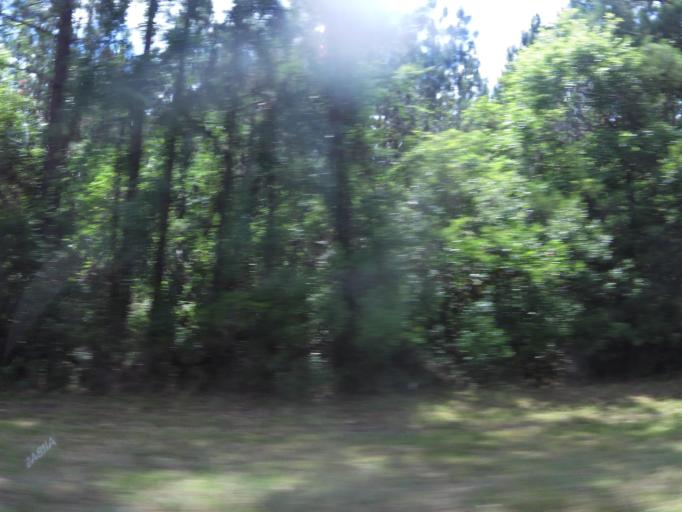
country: US
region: Florida
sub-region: Clay County
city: Green Cove Springs
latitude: 29.9545
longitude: -81.7392
